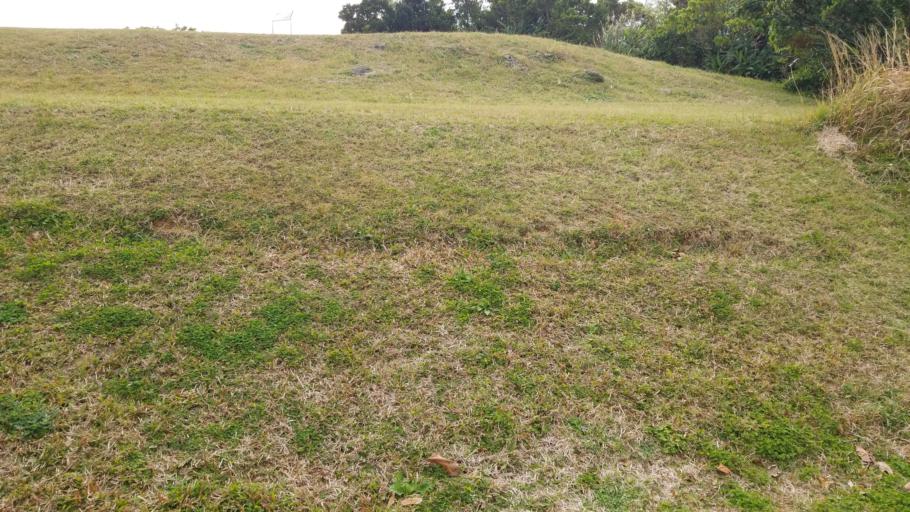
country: JP
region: Okinawa
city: Okinawa
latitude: 26.3413
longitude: 127.7856
